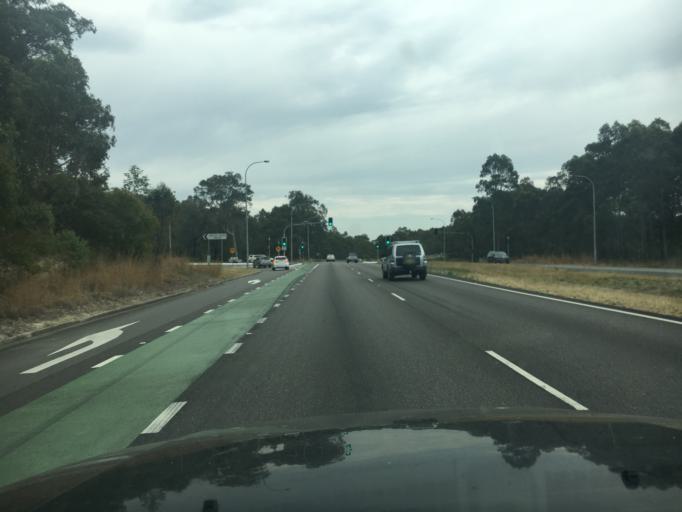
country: AU
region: New South Wales
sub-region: Maitland Municipality
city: East Maitland
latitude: -32.7737
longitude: 151.6087
